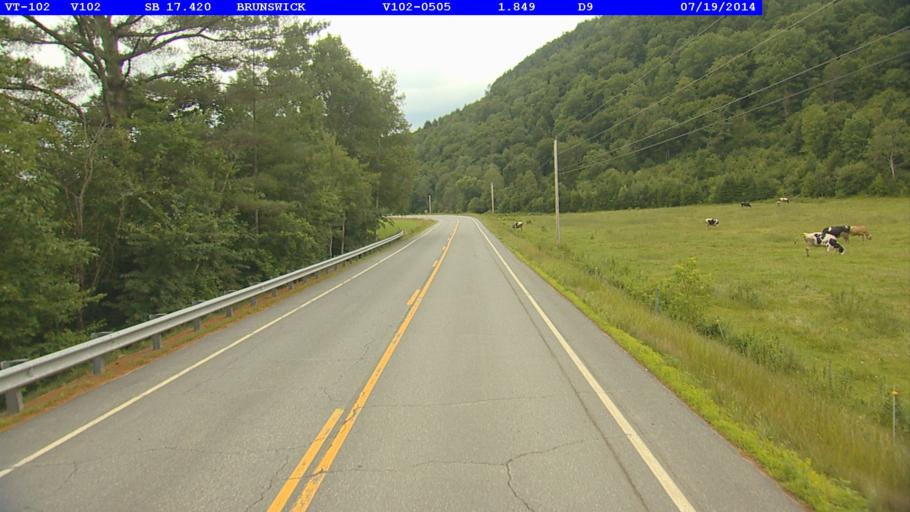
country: US
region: New Hampshire
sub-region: Coos County
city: Stratford
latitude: 44.6864
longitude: -71.6001
